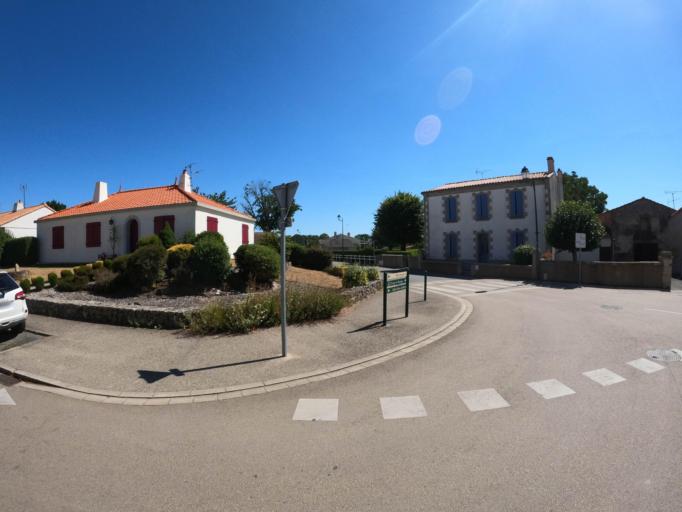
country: FR
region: Pays de la Loire
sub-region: Departement de la Vendee
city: Saint-Aubin-des-Ormeaux
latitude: 46.9730
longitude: -1.0516
